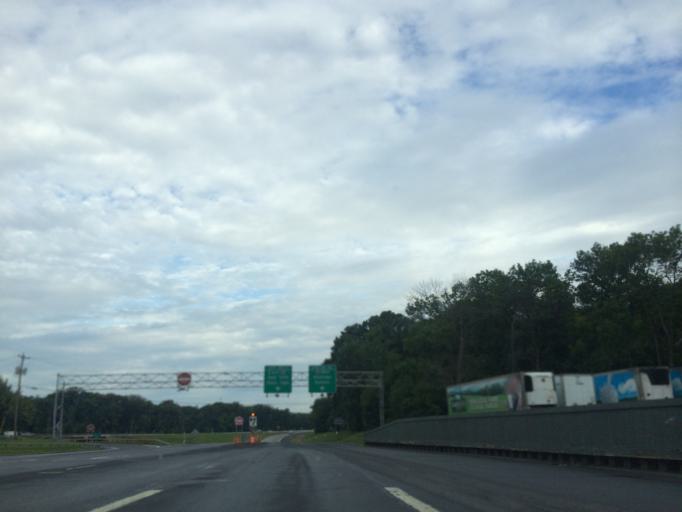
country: US
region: New York
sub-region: Albany County
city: Albany
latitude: 42.6334
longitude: -73.7784
